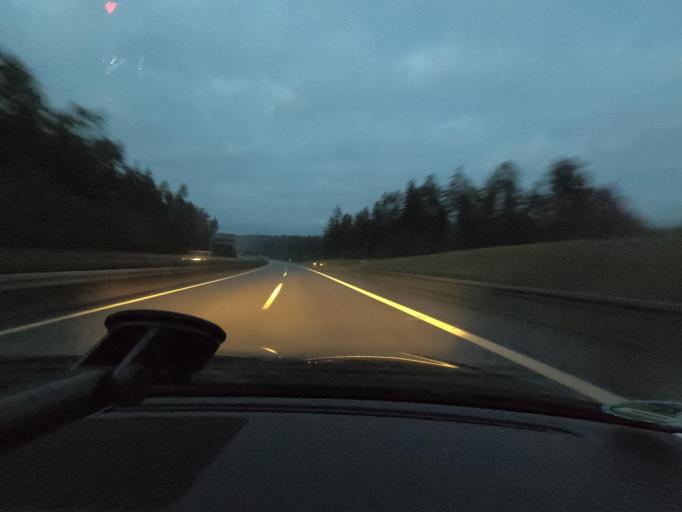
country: DE
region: Thuringia
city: Bockstadt
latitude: 50.3902
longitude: 10.9175
